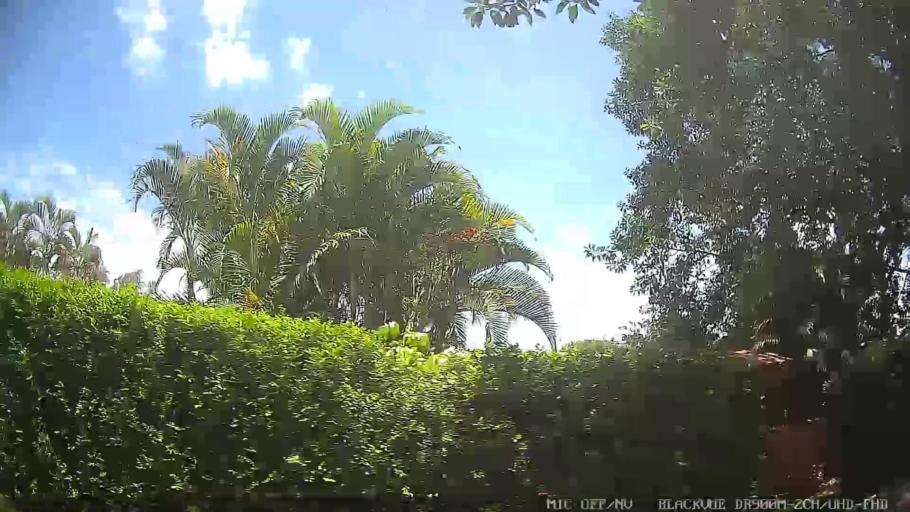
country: BR
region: Sao Paulo
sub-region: Laranjal Paulista
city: Laranjal Paulista
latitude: -23.0257
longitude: -47.8578
